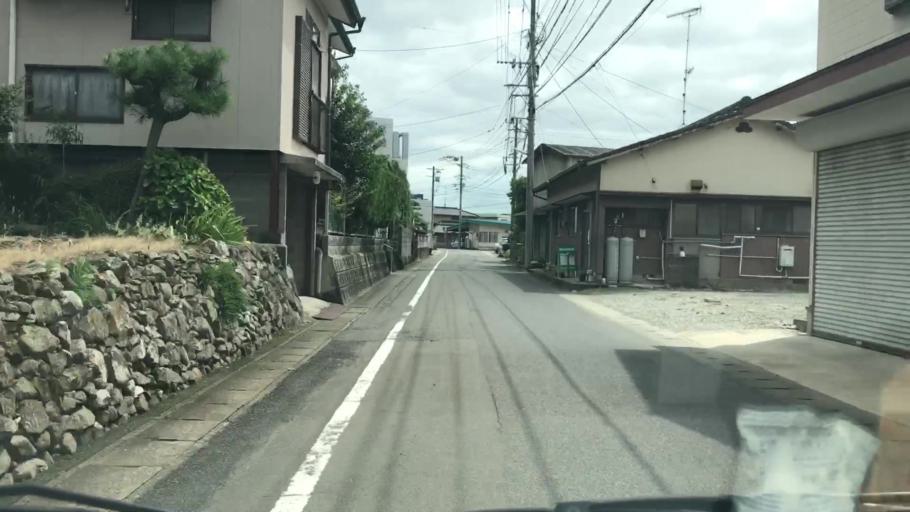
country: JP
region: Saga Prefecture
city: Kashima
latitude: 33.2222
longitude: 130.1573
